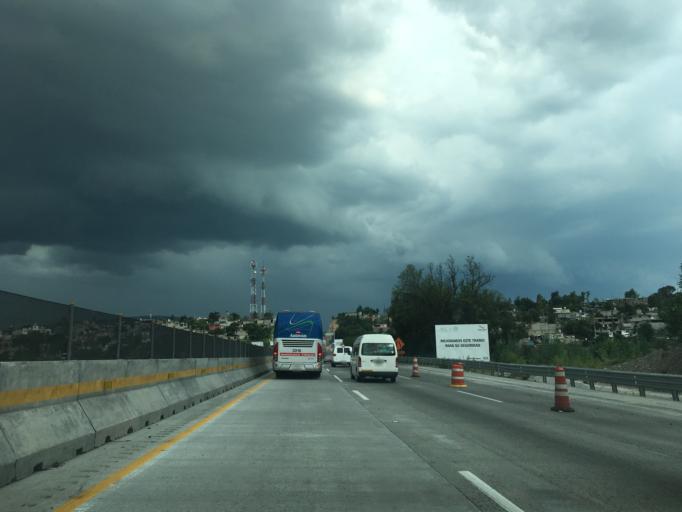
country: MX
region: Hidalgo
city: Tepeji de Ocampo
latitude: 19.9099
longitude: -99.3543
